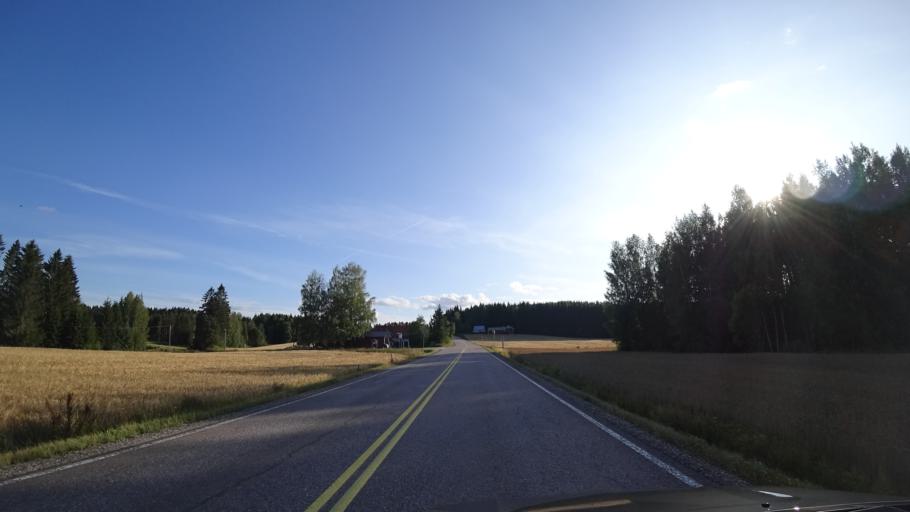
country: FI
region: Paijanne Tavastia
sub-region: Lahti
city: Asikkala
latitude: 61.1759
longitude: 25.3752
